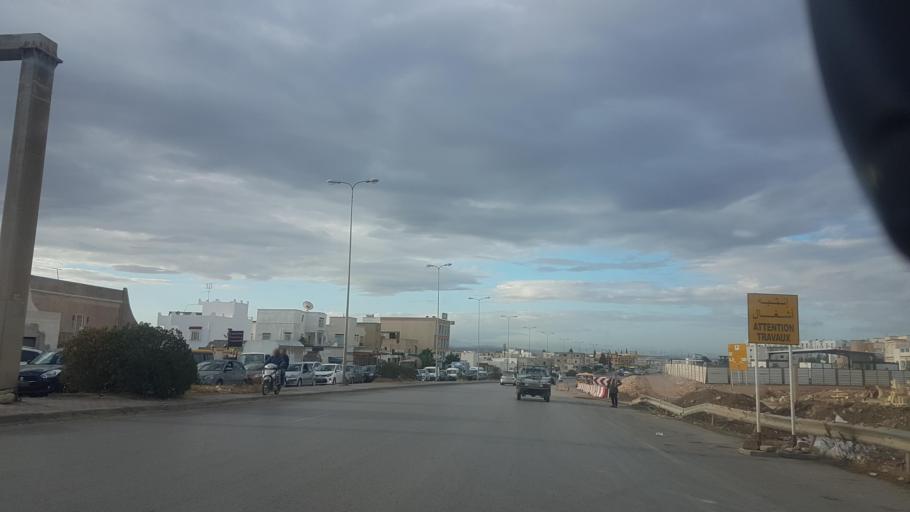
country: TN
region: Bin 'Arus
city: Ben Arous
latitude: 36.7435
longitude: 10.2078
